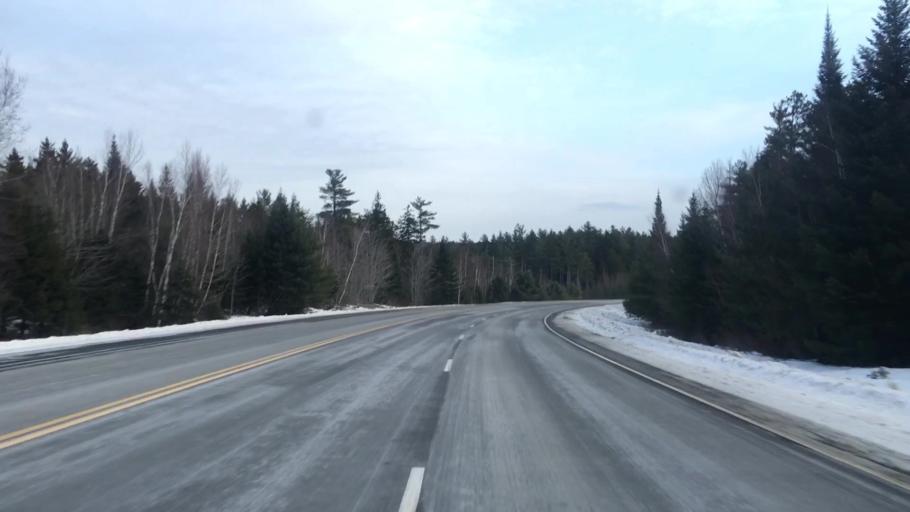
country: US
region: Maine
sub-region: Washington County
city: Addison
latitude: 44.9157
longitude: -67.7895
